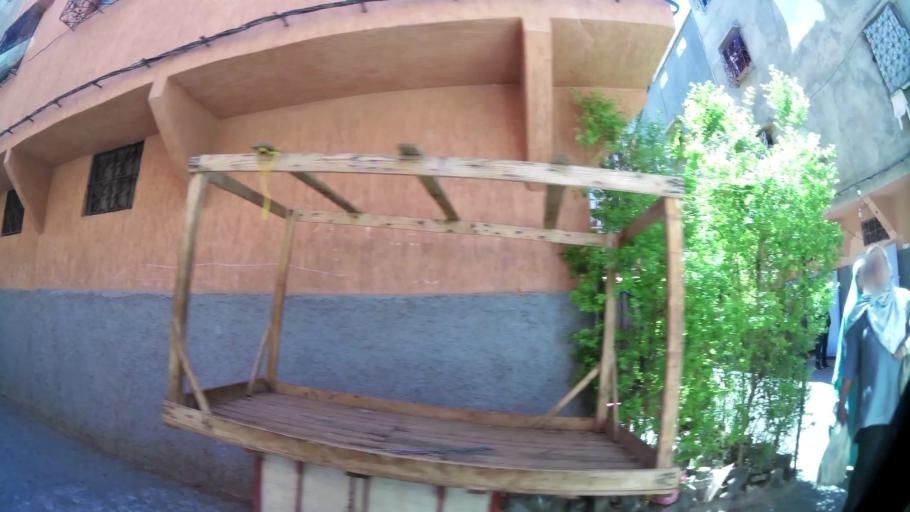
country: MA
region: Marrakech-Tensift-Al Haouz
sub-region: Marrakech
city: Marrakesh
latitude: 31.6552
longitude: -7.9946
